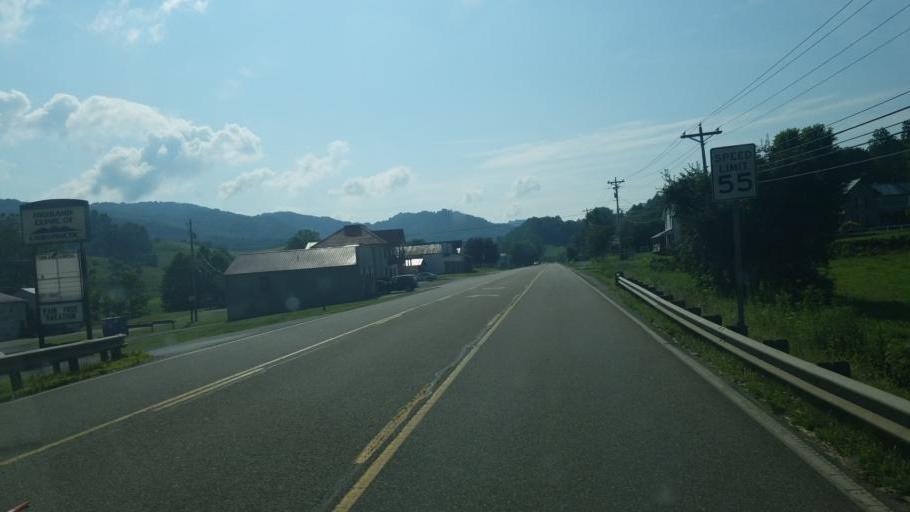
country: US
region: Tennessee
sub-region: Carter County
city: Roan Mountain
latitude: 36.1903
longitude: -82.0460
